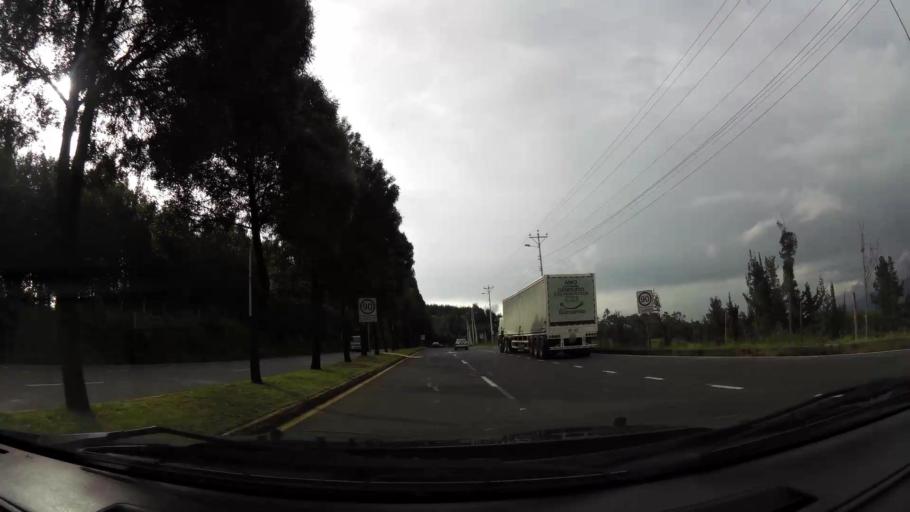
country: EC
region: Pichincha
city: Sangolqui
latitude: -0.3474
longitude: -78.5234
